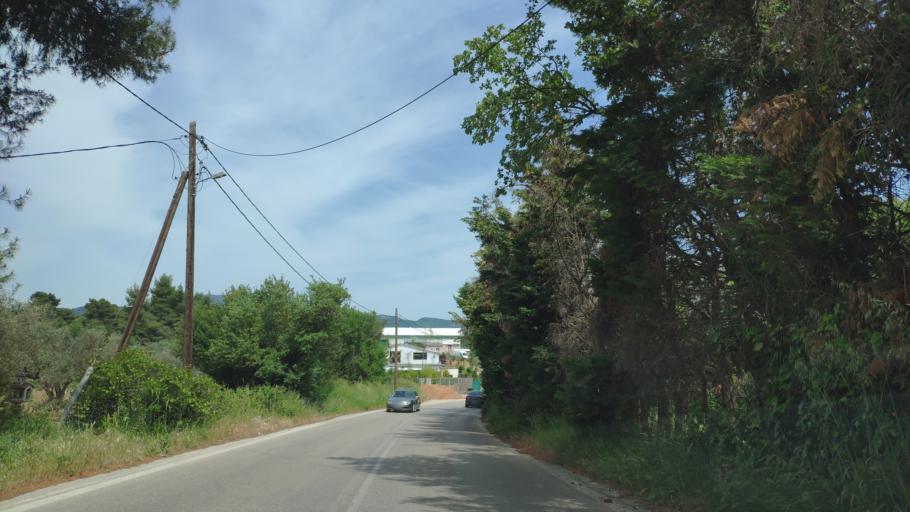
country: GR
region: Attica
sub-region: Nomarchia Anatolikis Attikis
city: Agios Stefanos
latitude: 38.1695
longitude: 23.8618
